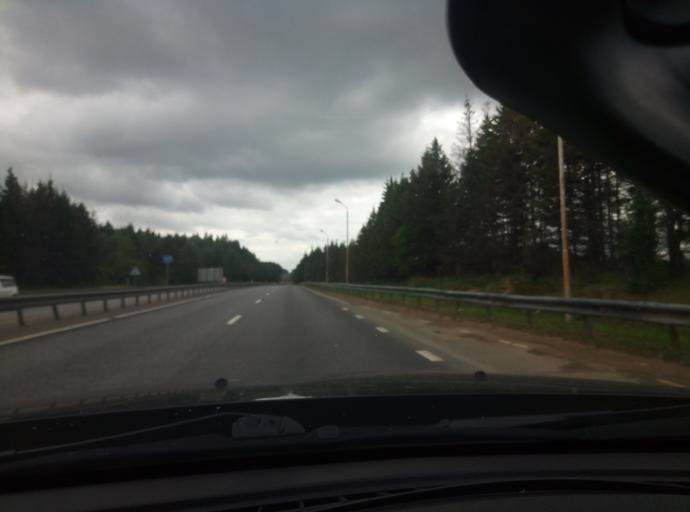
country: RU
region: Kaluga
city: Maloyaroslavets
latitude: 55.0065
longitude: 36.5379
